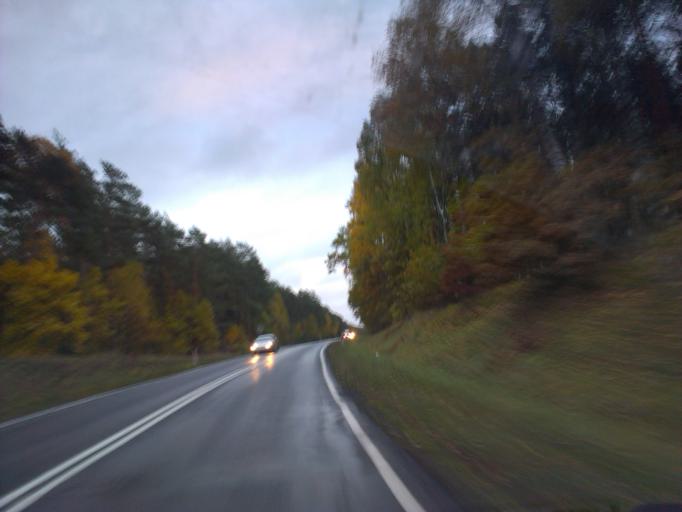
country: PL
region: Kujawsko-Pomorskie
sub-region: Powiat tucholski
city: Tuchola
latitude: 53.5545
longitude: 17.9074
